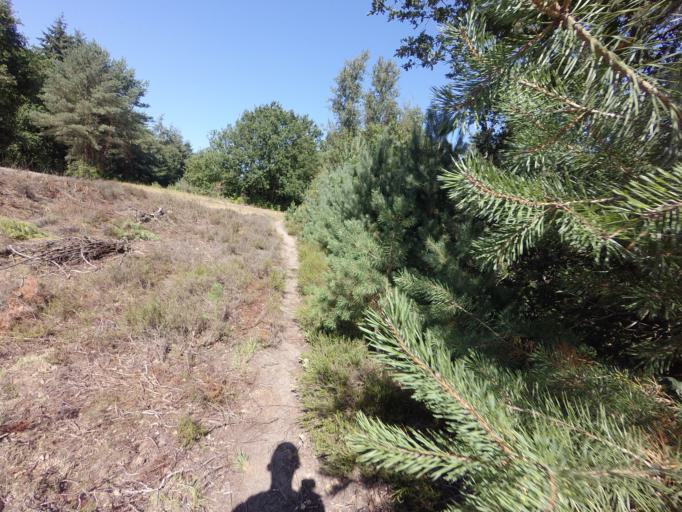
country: NL
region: Limburg
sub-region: Gemeente Roerdalen
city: Vlodrop
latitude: 51.1550
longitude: 6.1165
